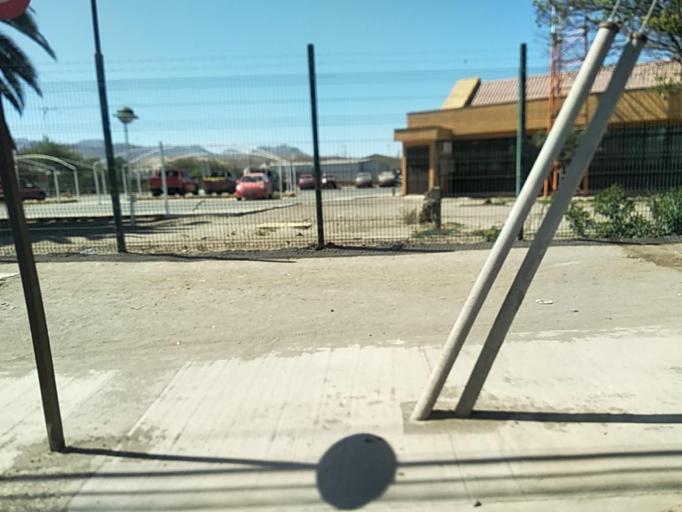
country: CL
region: Atacama
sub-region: Provincia de Copiapo
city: Copiapo
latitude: -27.4121
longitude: -70.2828
